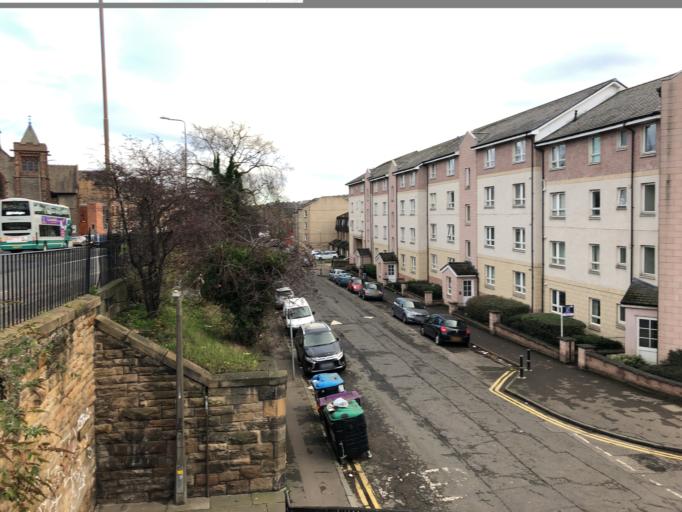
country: GB
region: Scotland
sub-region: West Lothian
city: Seafield
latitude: 55.9569
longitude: -3.1655
